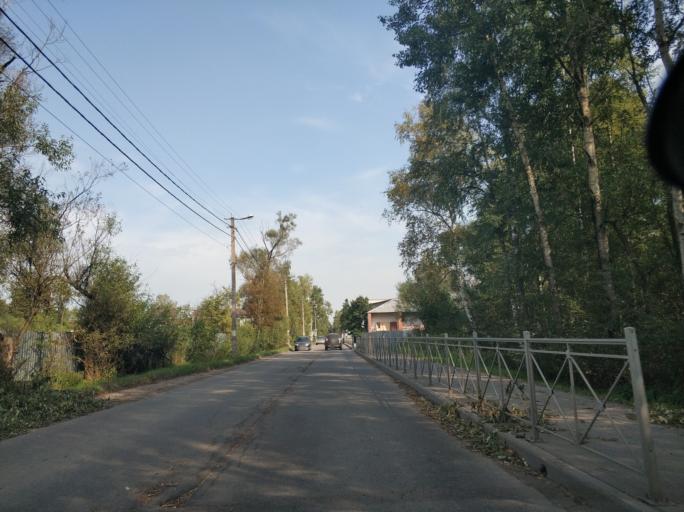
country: RU
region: Leningrad
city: Vsevolozhsk
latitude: 60.0197
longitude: 30.6774
